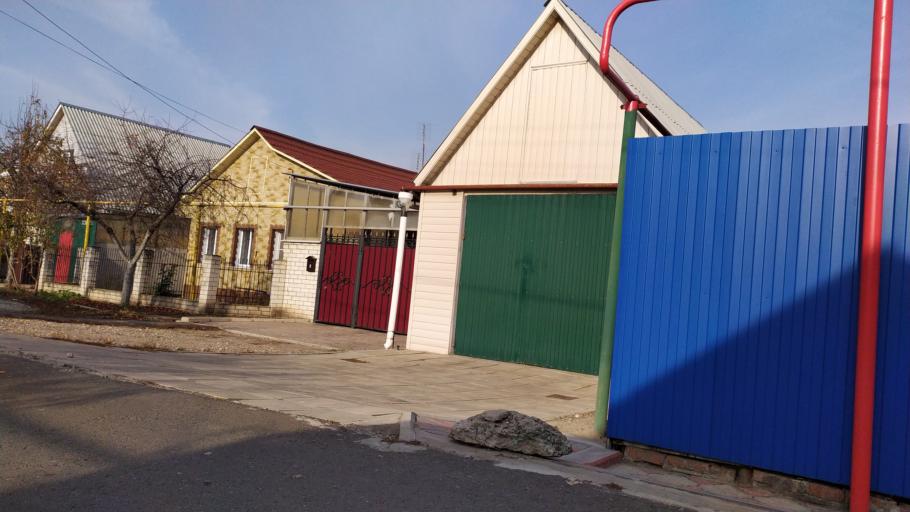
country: RU
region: Kursk
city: Kursk
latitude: 51.6441
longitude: 36.1471
